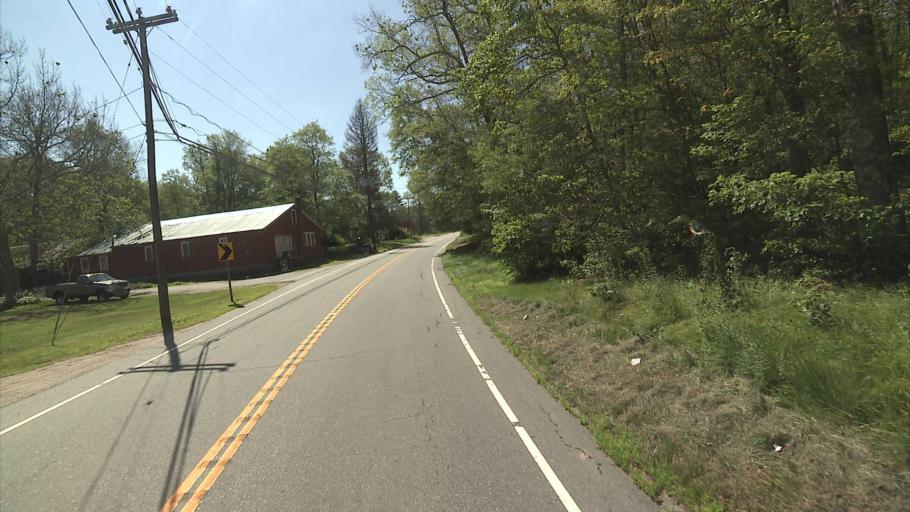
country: US
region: Connecticut
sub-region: Windham County
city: Moosup
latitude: 41.7169
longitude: -71.8467
